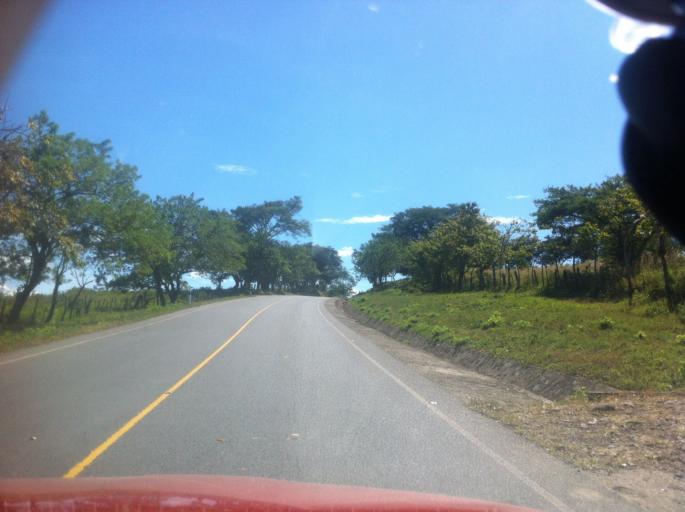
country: NI
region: Matagalpa
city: San Ramon
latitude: 12.8720
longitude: -85.8336
